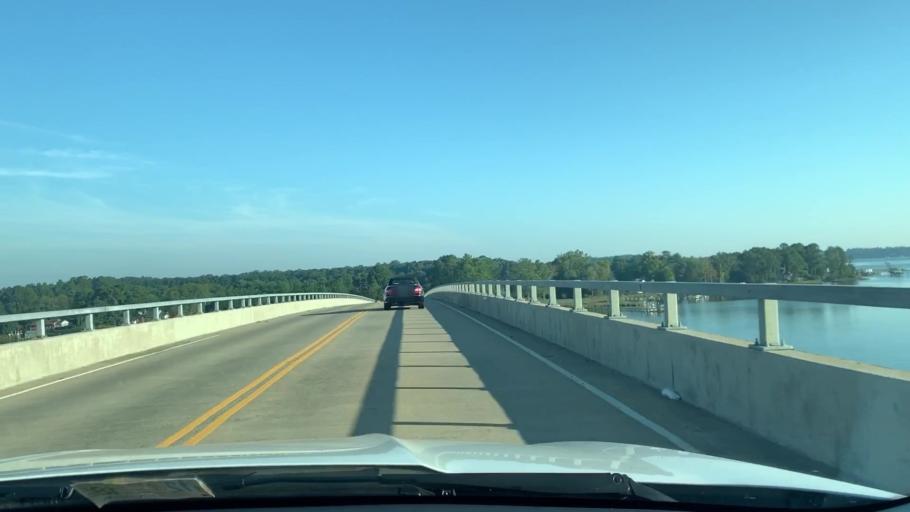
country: US
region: Virginia
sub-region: Middlesex County
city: Deltaville
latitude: 37.5100
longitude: -76.4200
